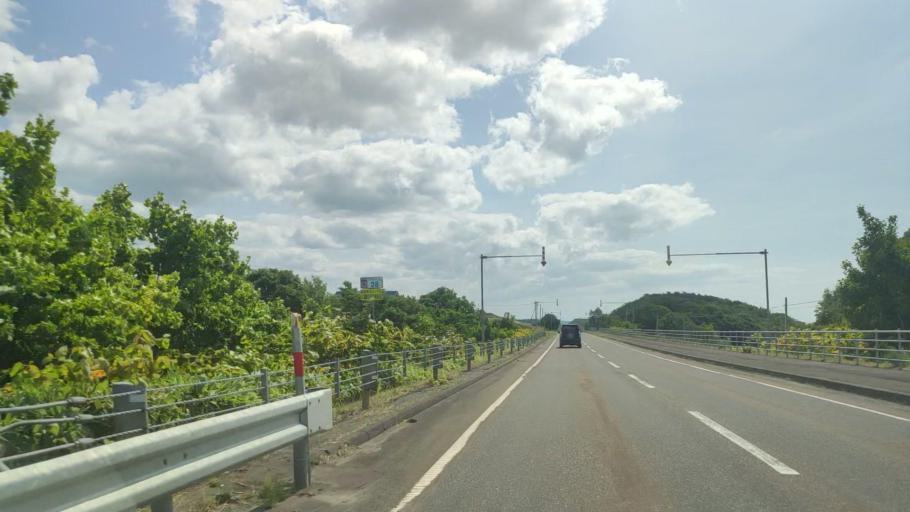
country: JP
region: Hokkaido
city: Makubetsu
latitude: 44.7827
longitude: 141.7906
